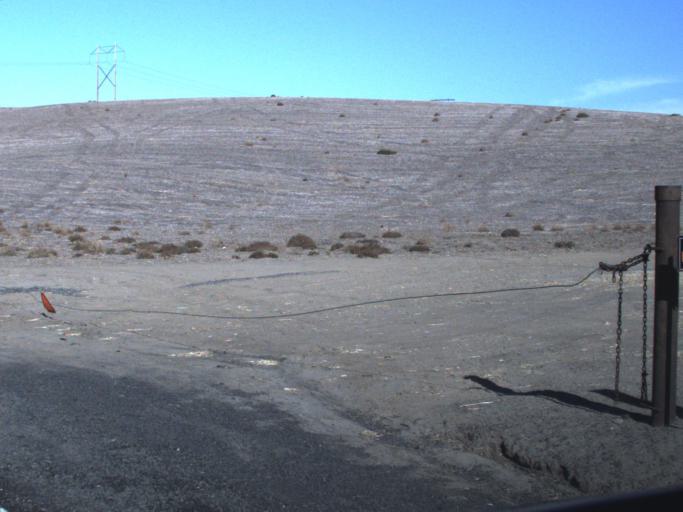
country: US
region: Washington
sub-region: Walla Walla County
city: Walla Walla
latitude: 46.1169
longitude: -118.3724
